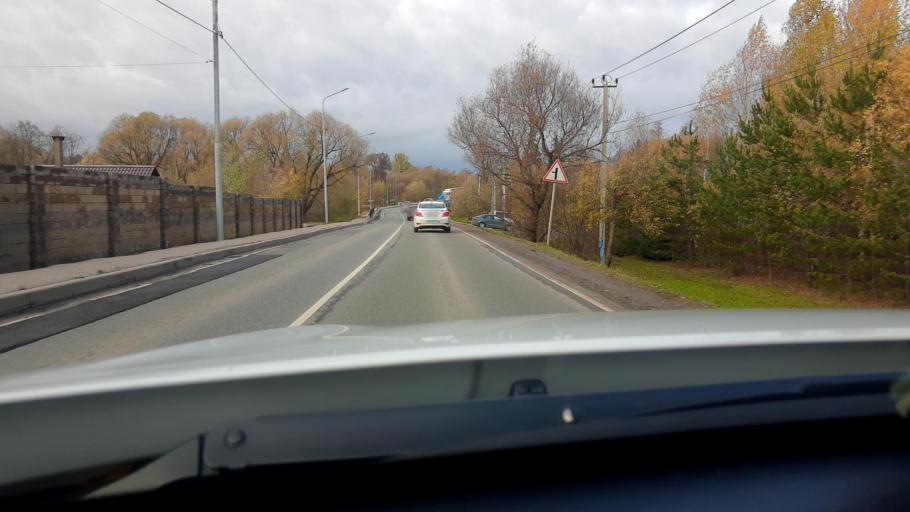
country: RU
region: Moskovskaya
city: Kokoshkino
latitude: 55.5322
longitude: 37.1529
